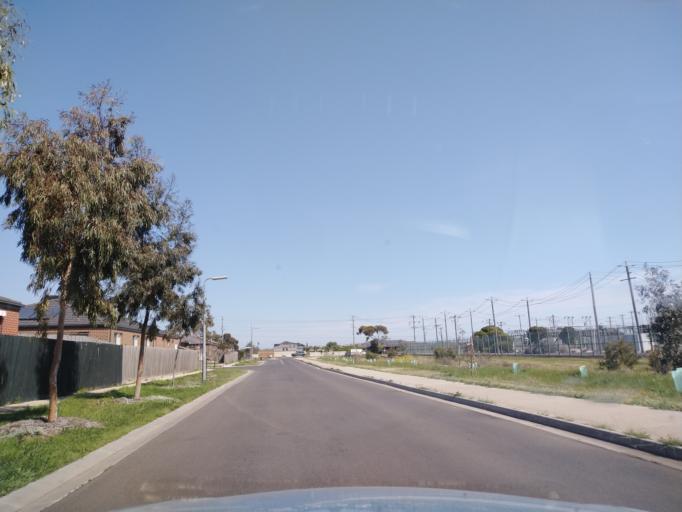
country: AU
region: Victoria
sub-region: Wyndham
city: Williams Landing
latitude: -37.8510
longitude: 144.7288
